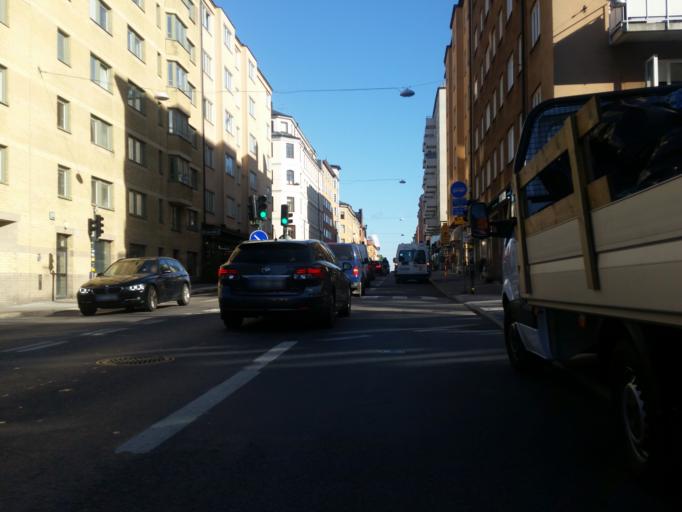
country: SE
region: Stockholm
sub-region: Stockholms Kommun
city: OEstermalm
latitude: 59.3129
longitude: 18.0851
